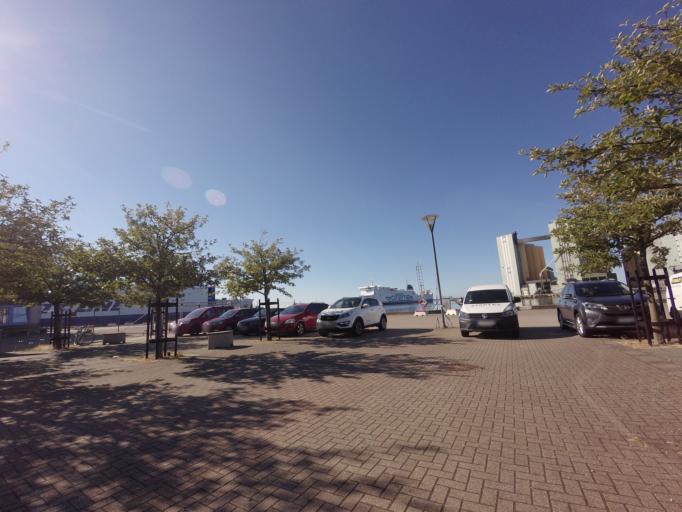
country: SE
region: Skane
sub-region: Ystads Kommun
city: Ystad
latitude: 55.4264
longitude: 13.8240
